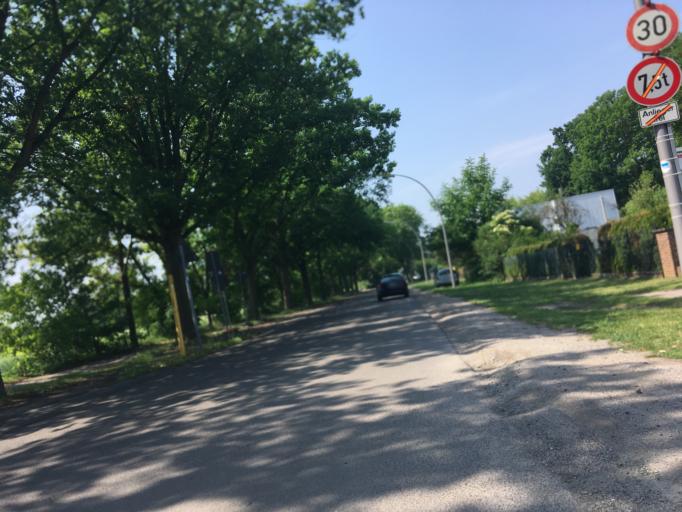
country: DE
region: Berlin
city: Heiligensee
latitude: 52.6136
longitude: 13.2245
